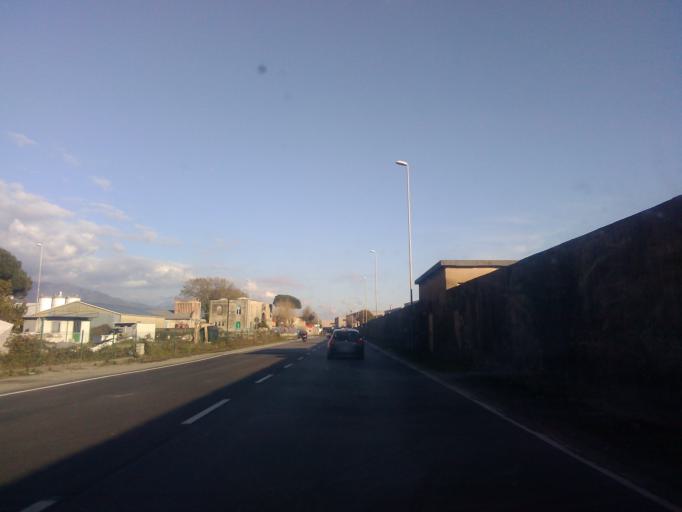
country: IT
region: Tuscany
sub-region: Provincia di Massa-Carrara
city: Carrara
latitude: 44.0415
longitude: 10.0667
